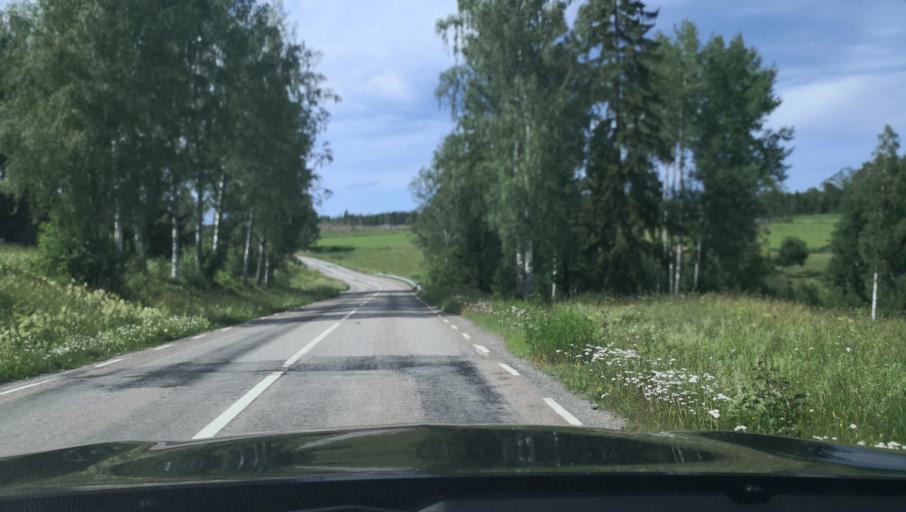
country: SE
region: Dalarna
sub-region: Avesta Kommun
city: Avesta
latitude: 59.9932
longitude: 16.1046
